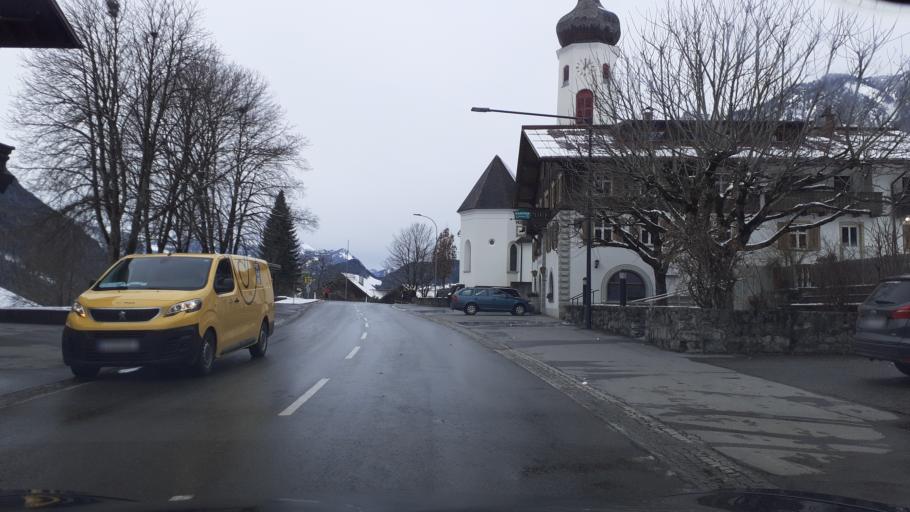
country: AT
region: Vorarlberg
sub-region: Politischer Bezirk Bludenz
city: Innerbraz
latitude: 47.1447
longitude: 9.9181
